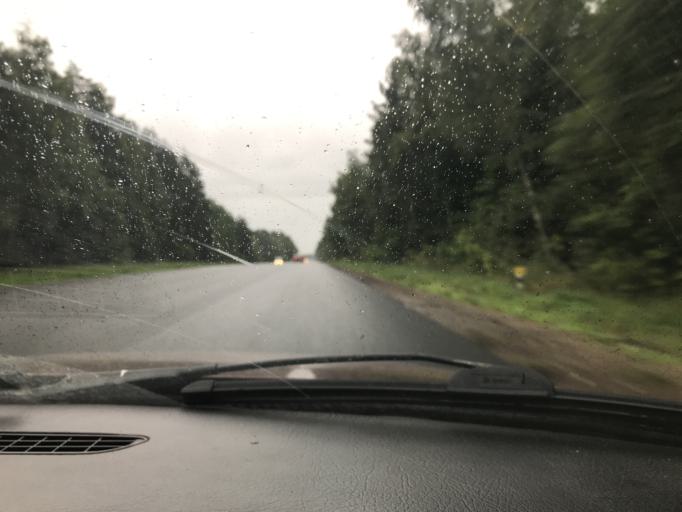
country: RU
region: Kaluga
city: Kurovskoye
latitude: 54.5974
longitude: 36.0549
